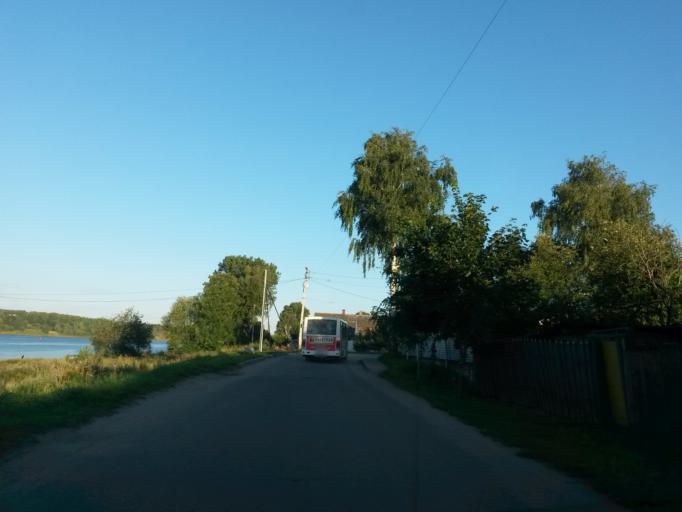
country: RU
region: Jaroslavl
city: Tutayev
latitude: 57.8722
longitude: 39.5383
